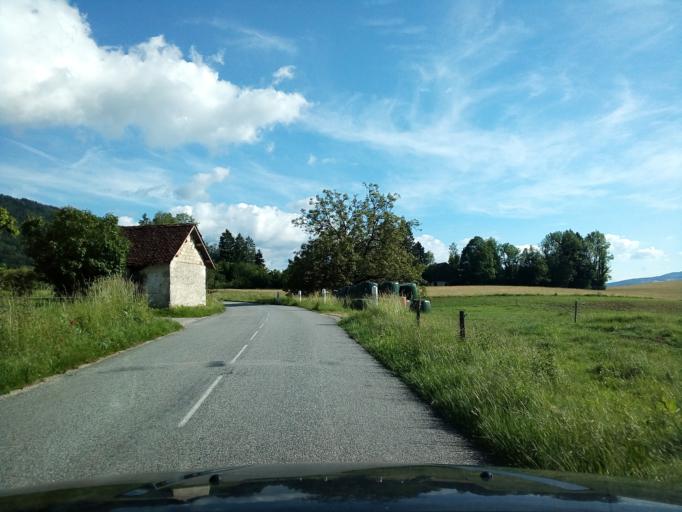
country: FR
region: Rhone-Alpes
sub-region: Departement de la Savoie
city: Saint-Beron
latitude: 45.4964
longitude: 5.7698
